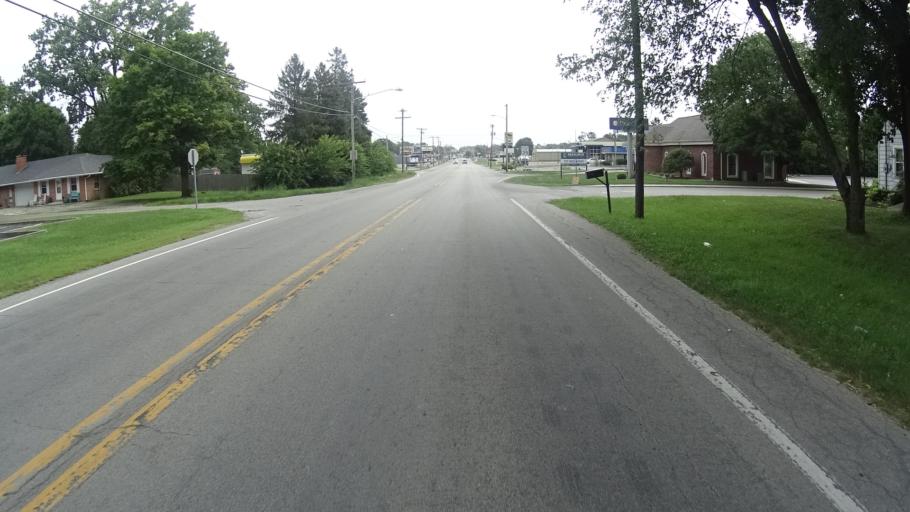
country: US
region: Indiana
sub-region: Madison County
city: Edgewood
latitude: 40.1016
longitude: -85.7217
